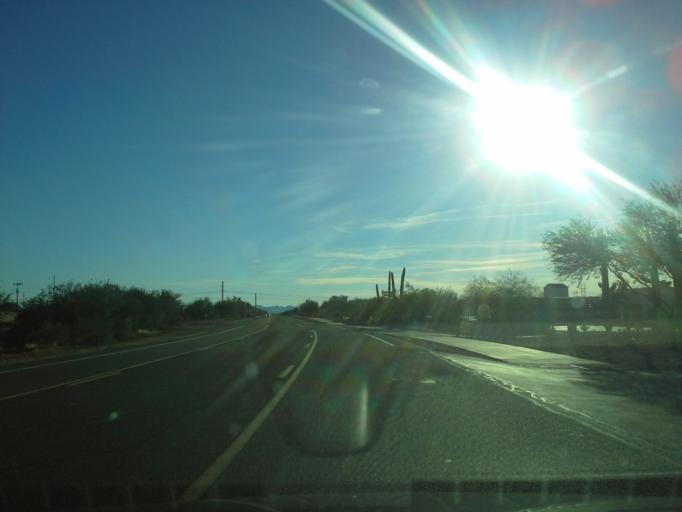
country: US
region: Arizona
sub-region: Pinal County
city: Apache Junction
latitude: 33.3584
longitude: -111.4506
